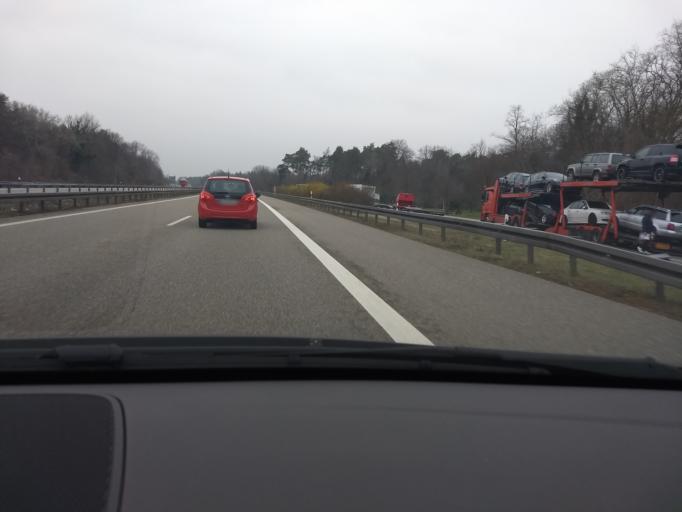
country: DE
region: Baden-Wuerttemberg
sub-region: Freiburg Region
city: Bad Bellingen
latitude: 47.7450
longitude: 7.5513
